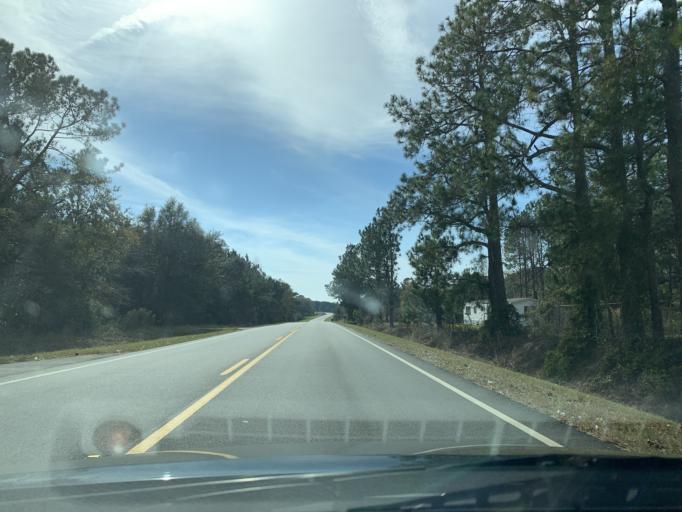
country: US
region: Georgia
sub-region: Turner County
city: Ashburn
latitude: 31.7354
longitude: -83.5755
